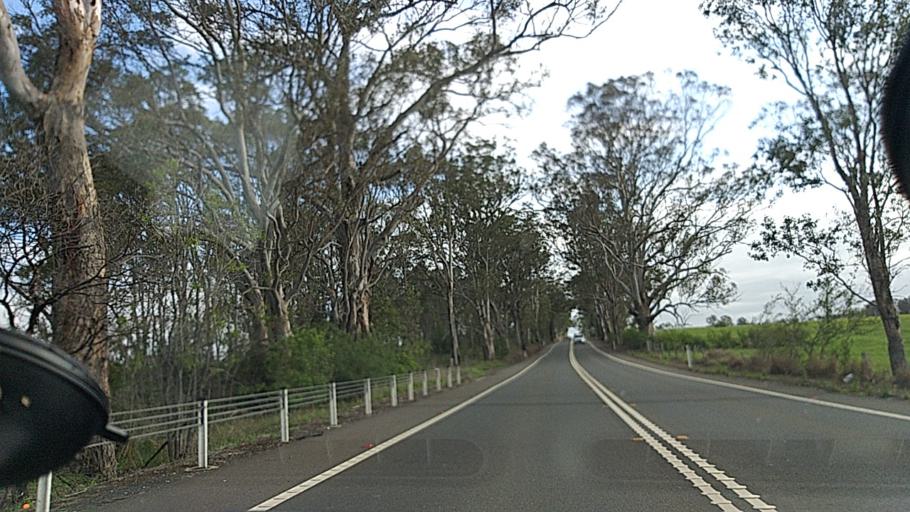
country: AU
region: New South Wales
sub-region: Campbelltown Municipality
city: Glen Alpine
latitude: -34.1208
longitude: 150.7961
